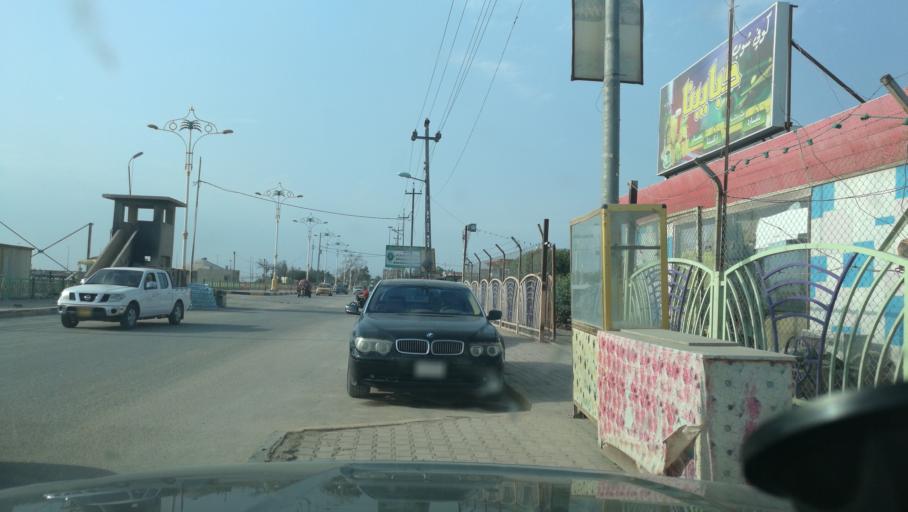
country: IQ
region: Basra Governorate
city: Al Basrah al Qadimah
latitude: 30.5217
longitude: 47.8478
